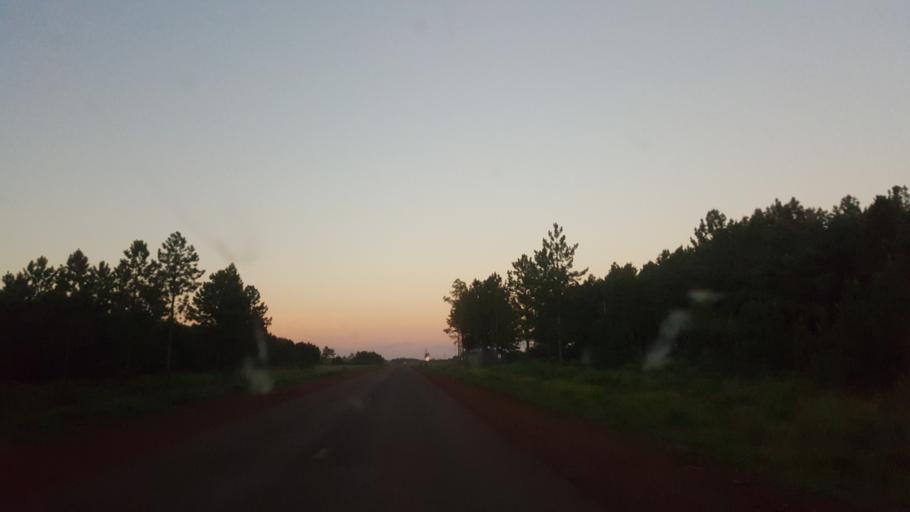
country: AR
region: Corrientes
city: Garruchos
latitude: -28.2215
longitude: -55.7975
